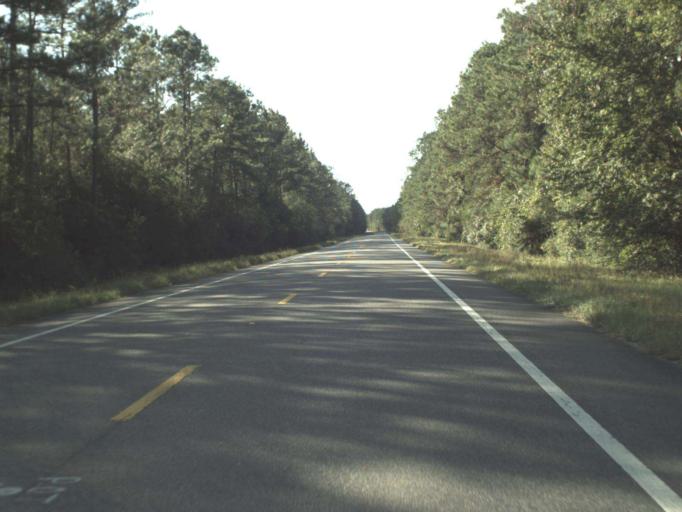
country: US
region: Florida
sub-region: Bay County
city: Laguna Beach
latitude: 30.4451
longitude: -85.8312
